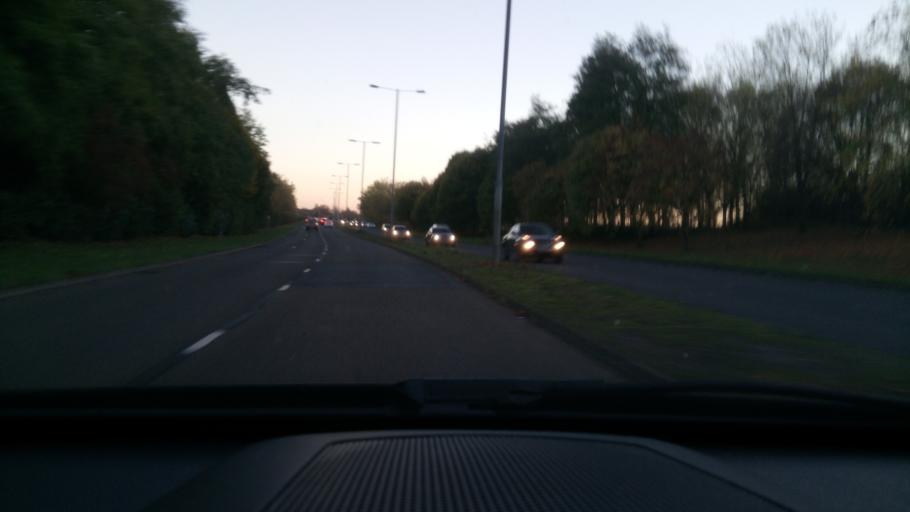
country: GB
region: England
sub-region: Peterborough
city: Peterborough
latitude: 52.5864
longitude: -0.2552
